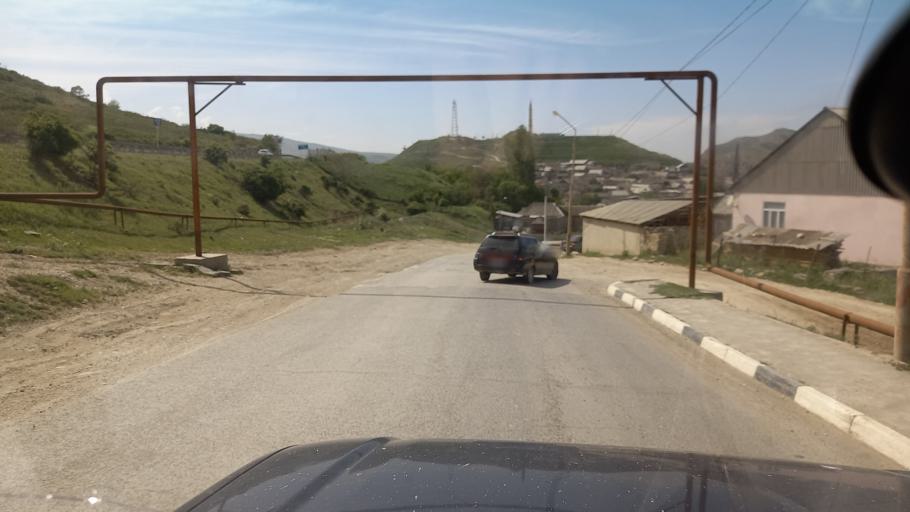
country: RU
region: Dagestan
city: Karabudakhkent
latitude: 42.7066
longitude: 47.5726
